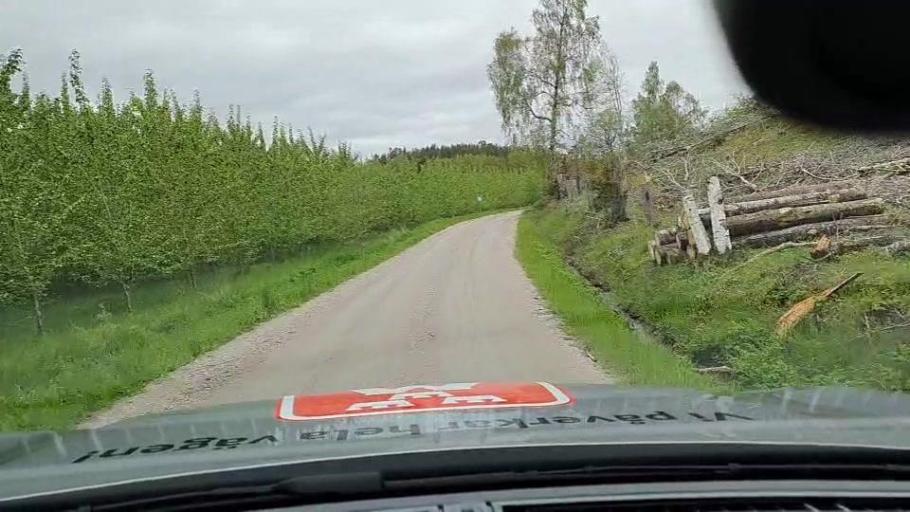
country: SE
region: Soedermanland
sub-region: Nykopings Kommun
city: Svalsta
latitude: 58.6288
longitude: 16.9387
